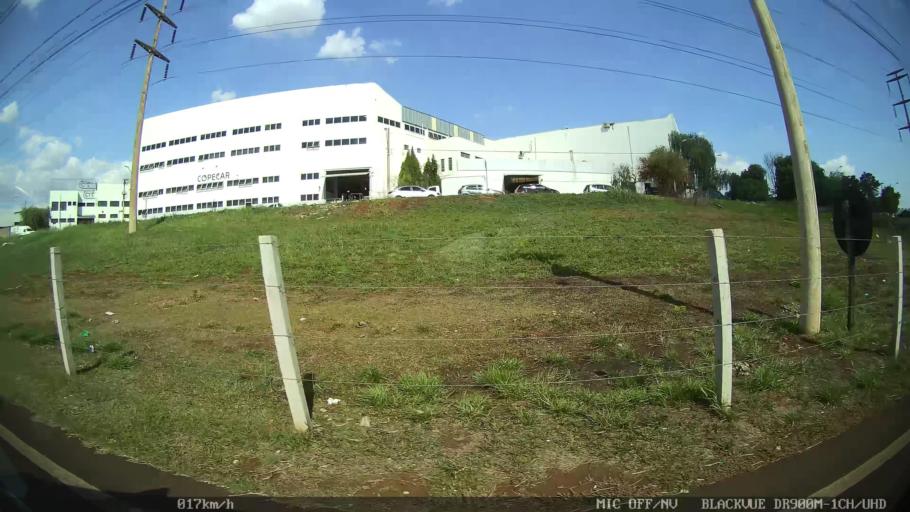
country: BR
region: Sao Paulo
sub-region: Ribeirao Preto
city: Ribeirao Preto
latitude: -21.1790
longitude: -47.8368
